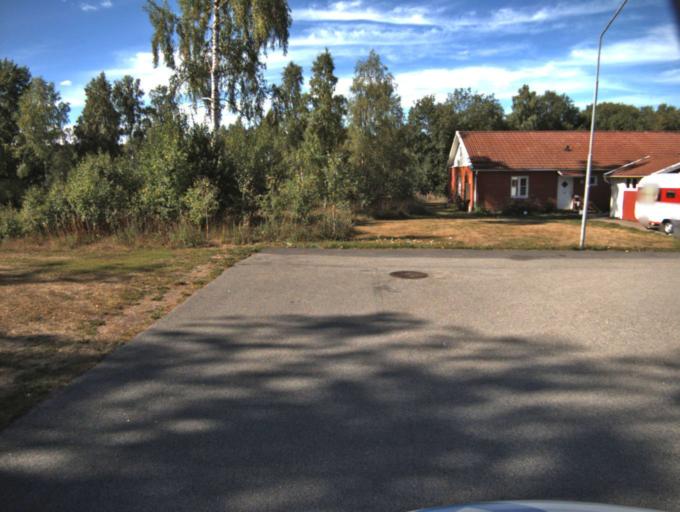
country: SE
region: Vaestra Goetaland
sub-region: Ulricehamns Kommun
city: Ulricehamn
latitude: 57.6954
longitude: 13.5784
